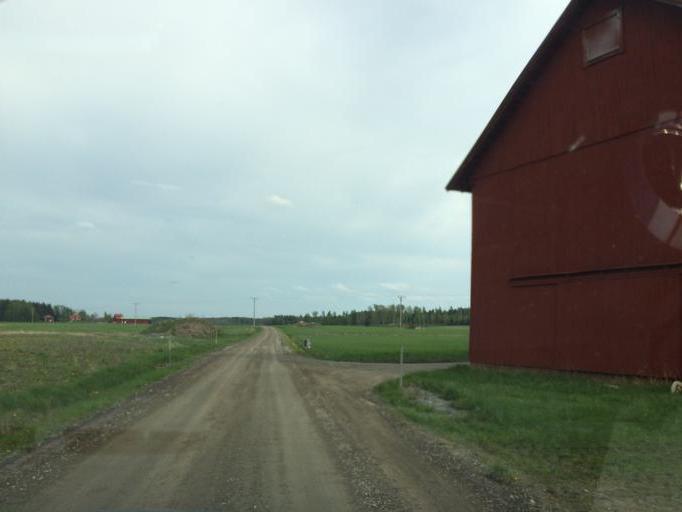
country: SE
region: Vaestmanland
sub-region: Kopings Kommun
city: Koping
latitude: 59.6101
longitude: 16.0628
